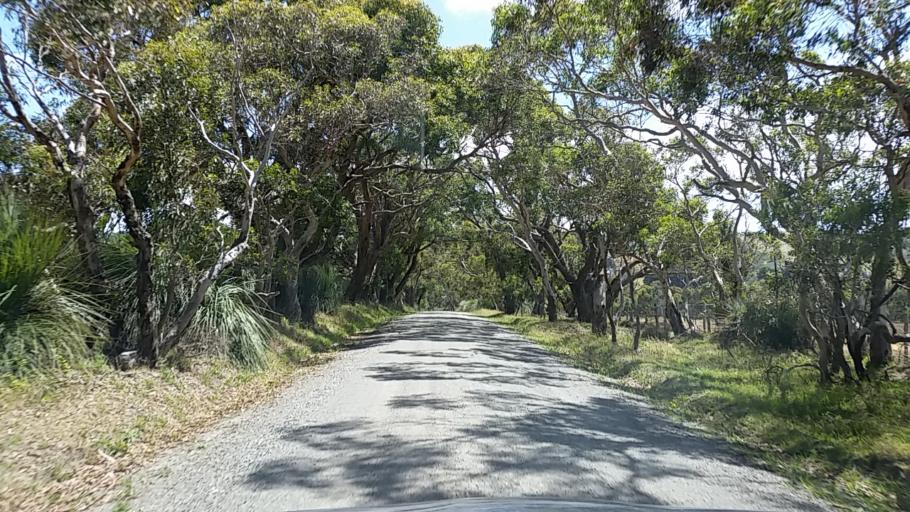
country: AU
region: South Australia
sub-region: Alexandrina
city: Mount Compass
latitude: -35.4368
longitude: 138.5866
